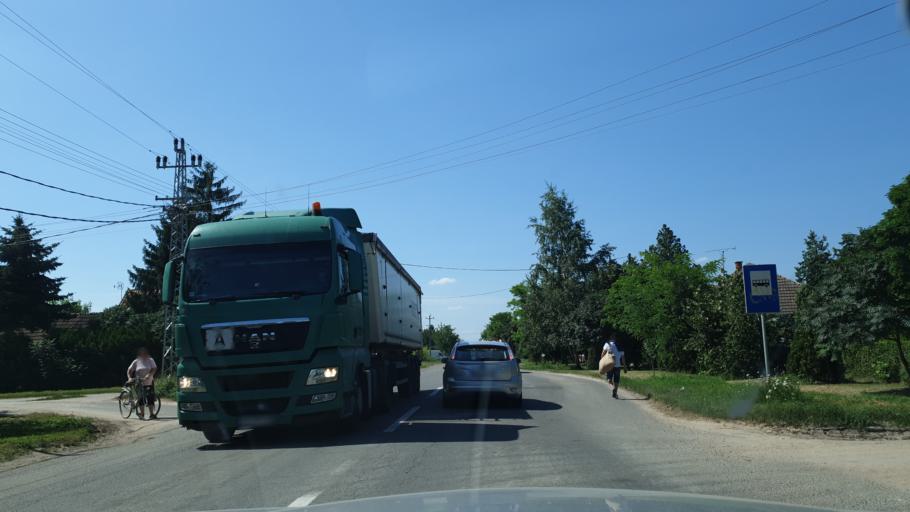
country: HU
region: Bacs-Kiskun
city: Kelebia
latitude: 46.1428
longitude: 19.5882
